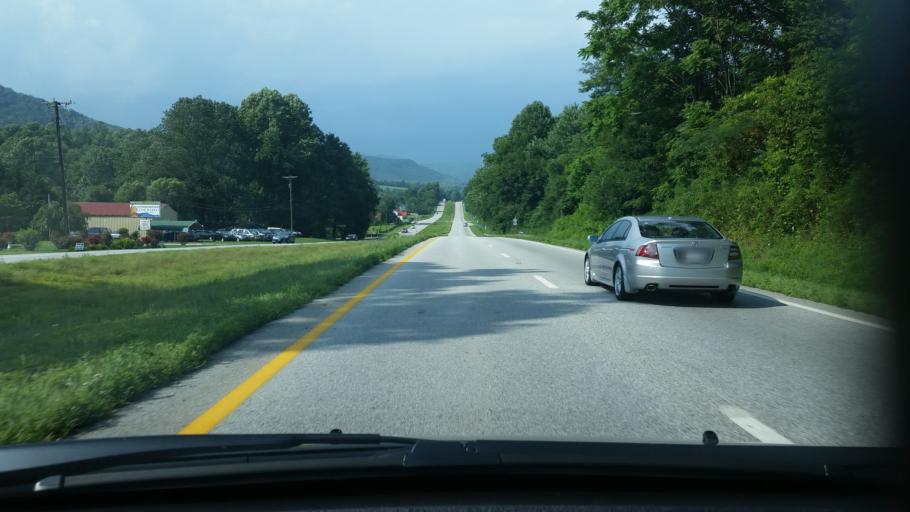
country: US
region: Virginia
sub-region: Nelson County
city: Lovingston
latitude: 37.7765
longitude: -78.8692
